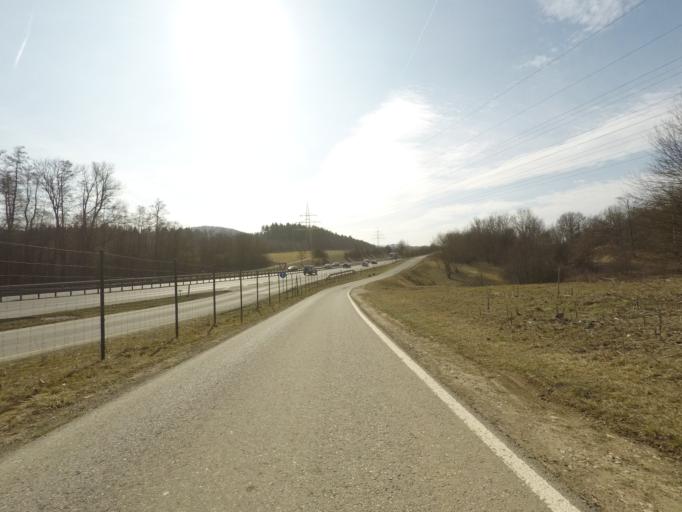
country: DE
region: Baden-Wuerttemberg
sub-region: Tuebingen Region
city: Metzingen
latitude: 48.5217
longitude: 9.2517
